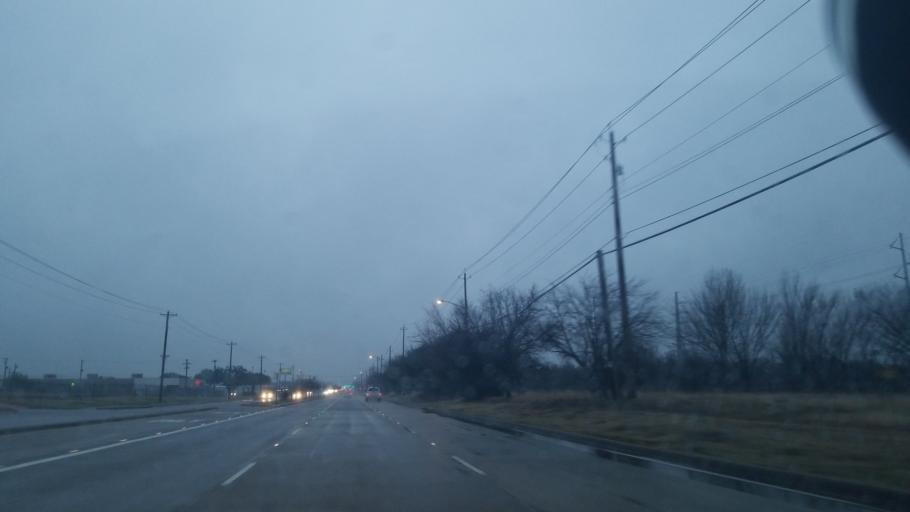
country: US
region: Texas
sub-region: Denton County
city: Denton
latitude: 33.2227
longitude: -97.0902
